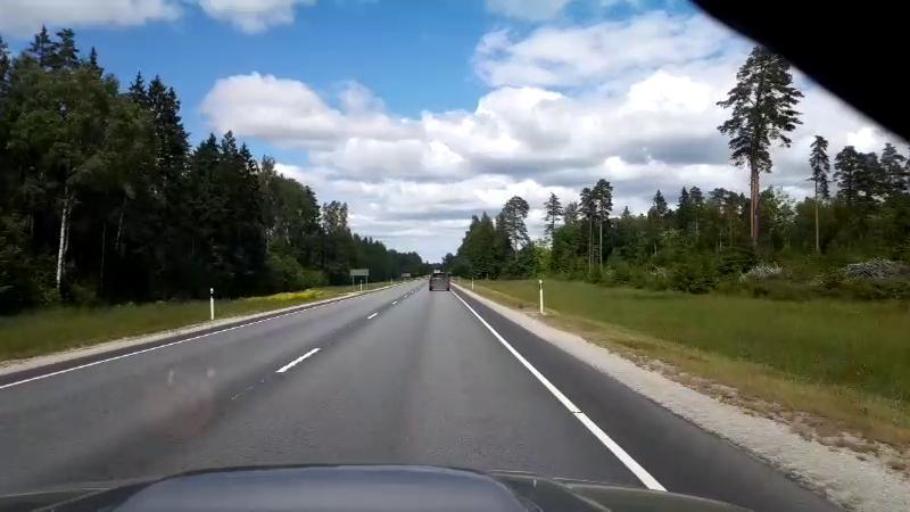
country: EE
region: Harju
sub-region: Nissi vald
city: Riisipere
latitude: 59.0965
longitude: 24.4674
